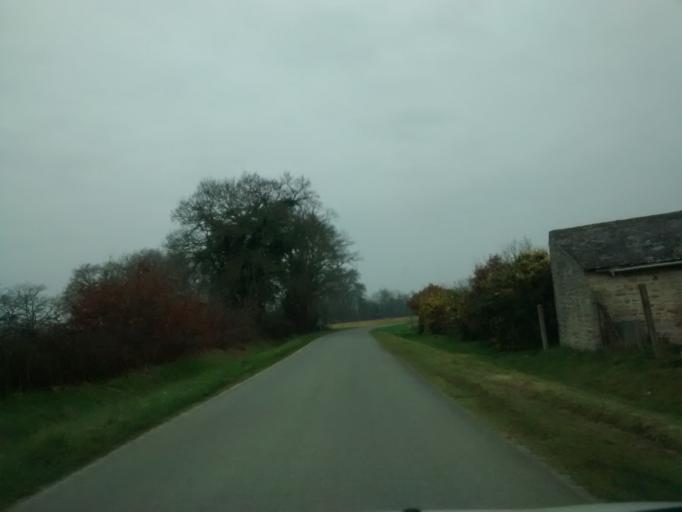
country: FR
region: Brittany
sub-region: Departement d'Ille-et-Vilaine
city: Sens-de-Bretagne
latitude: 48.3691
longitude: -1.5043
